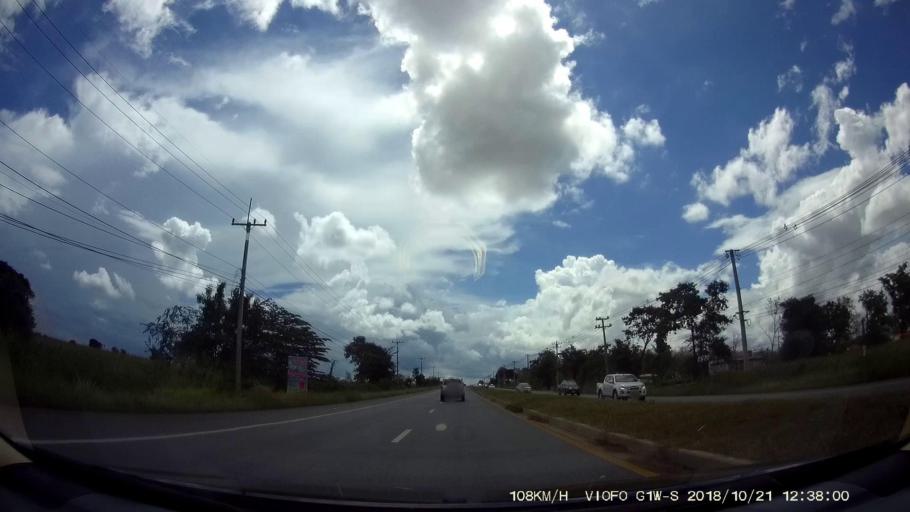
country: TH
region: Nakhon Ratchasima
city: Amphoe Sikhiu
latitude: 15.0604
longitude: 101.7083
